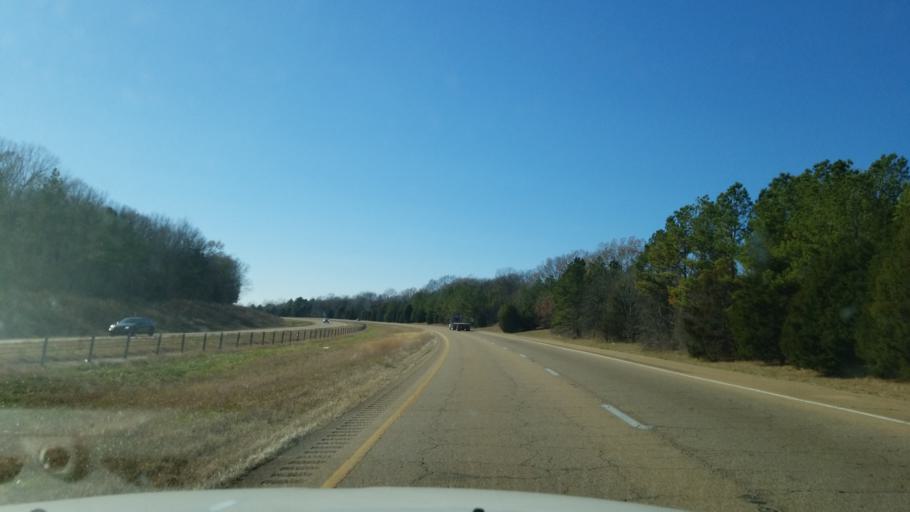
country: US
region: Mississippi
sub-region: Oktibbeha County
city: Starkville
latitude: 33.4845
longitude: -88.7139
